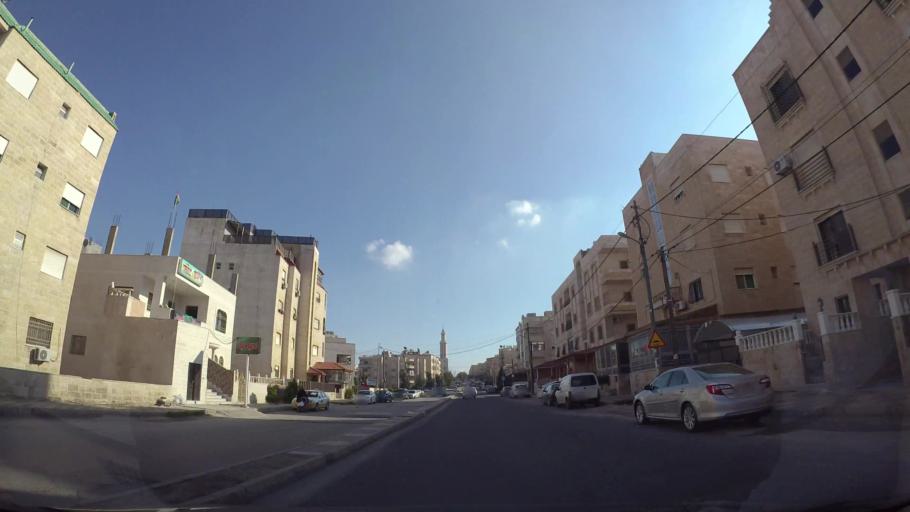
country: JO
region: Amman
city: Amman
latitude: 31.9824
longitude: 35.9460
